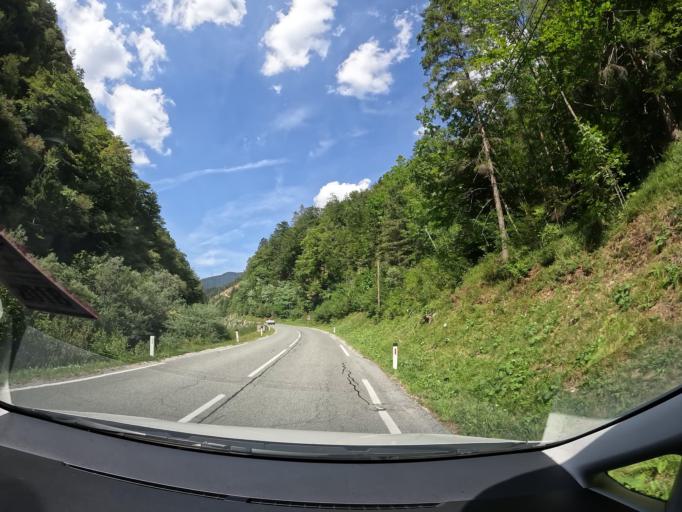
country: SI
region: Cerklje na Gorenjskem
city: Cerklje na Gorenjskem
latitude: 46.3149
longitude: 14.4997
